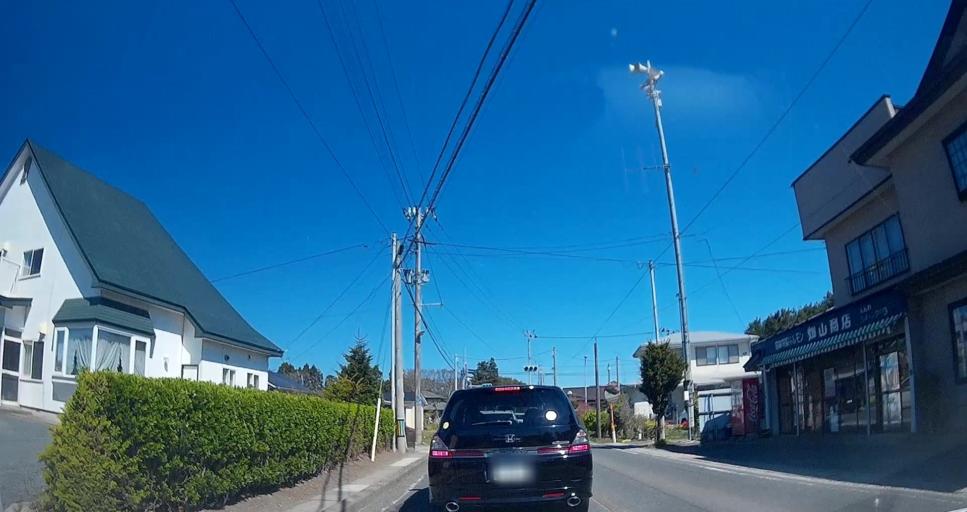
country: JP
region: Aomori
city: Misawa
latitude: 40.6771
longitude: 141.4300
